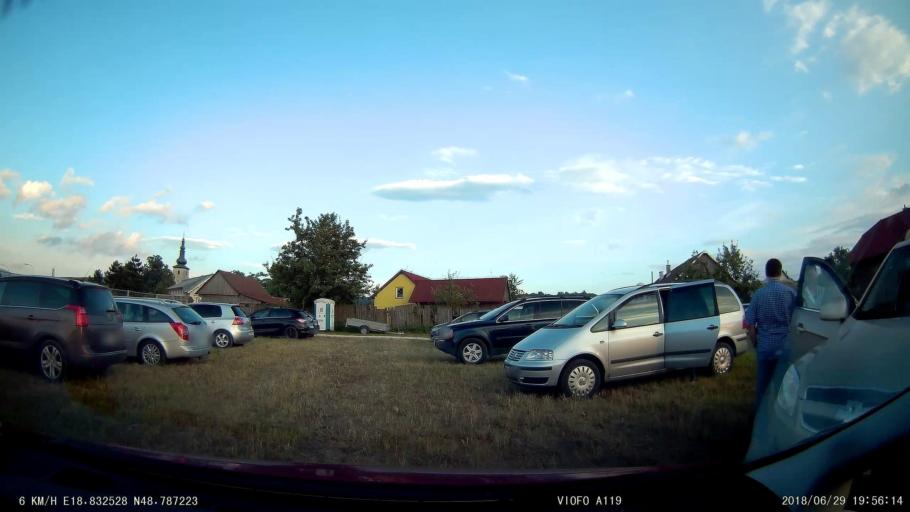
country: SK
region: Nitriansky
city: Handlova
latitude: 48.7871
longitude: 18.8327
